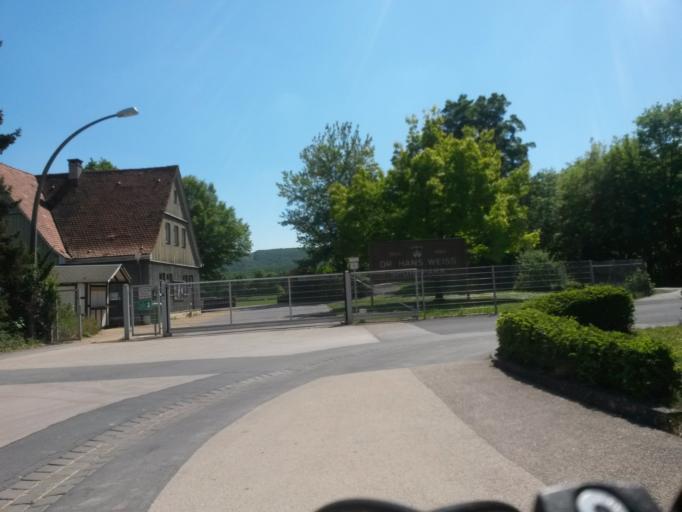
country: DE
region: Bavaria
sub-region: Regierungsbezirk Unterfranken
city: Bad Kissingen
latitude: 50.1858
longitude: 10.0742
